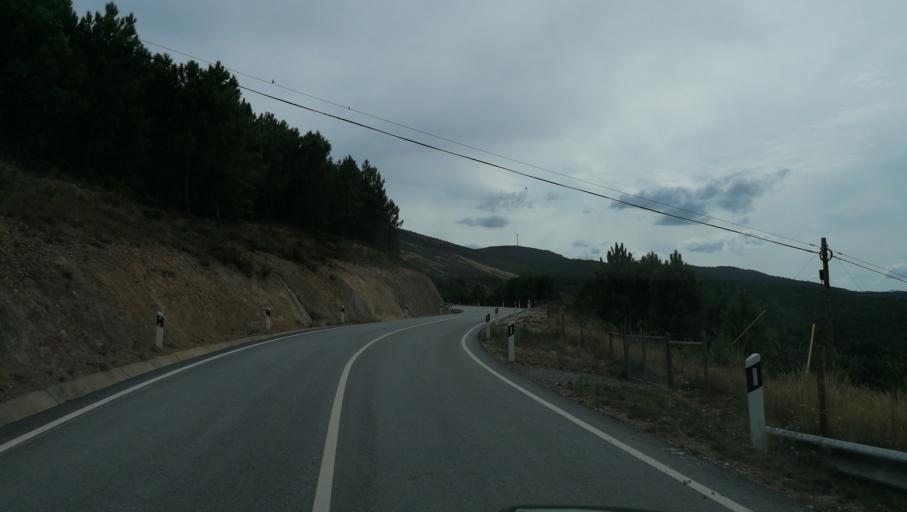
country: PT
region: Vila Real
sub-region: Vila Pouca de Aguiar
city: Vila Pouca de Aguiar
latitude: 41.5613
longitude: -7.7047
